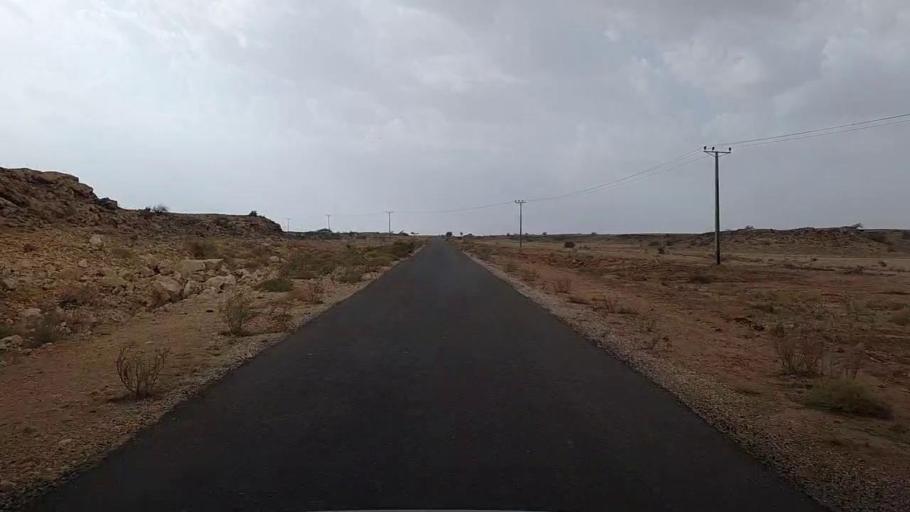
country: PK
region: Sindh
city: Jamshoro
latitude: 25.4291
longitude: 67.6884
